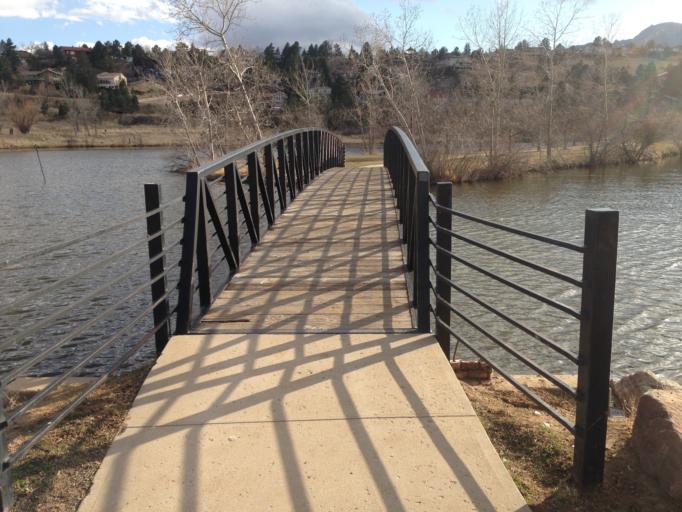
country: US
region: Colorado
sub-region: Boulder County
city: Boulder
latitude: 39.9727
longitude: -105.2495
